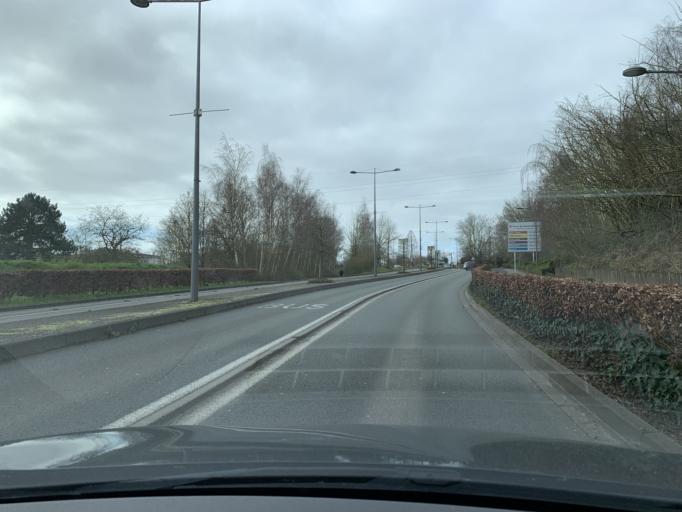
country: FR
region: Nord-Pas-de-Calais
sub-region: Departement du Nord
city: Waziers
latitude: 50.3821
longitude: 3.0956
